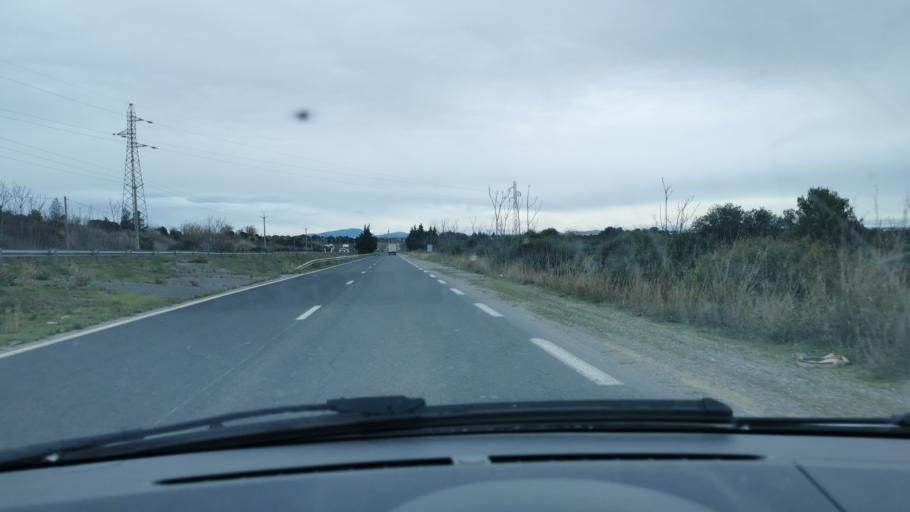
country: FR
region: Languedoc-Roussillon
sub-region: Departement de l'Herault
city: Mireval
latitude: 43.5366
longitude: 3.8230
